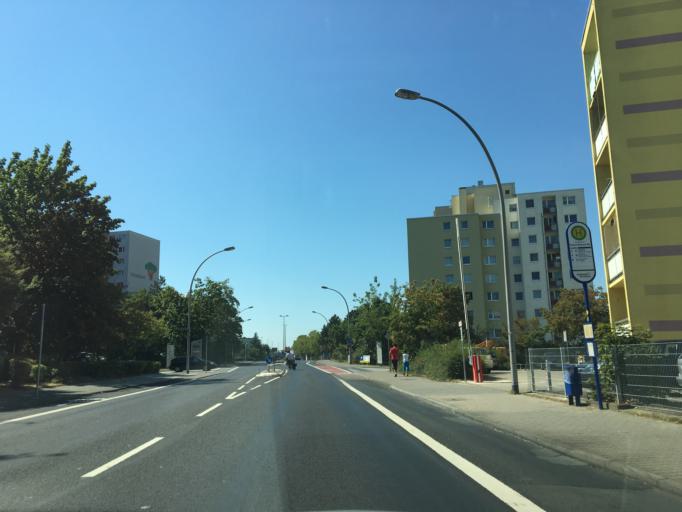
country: DE
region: Hesse
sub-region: Regierungsbezirk Darmstadt
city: Russelsheim
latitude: 49.9789
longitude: 8.4384
